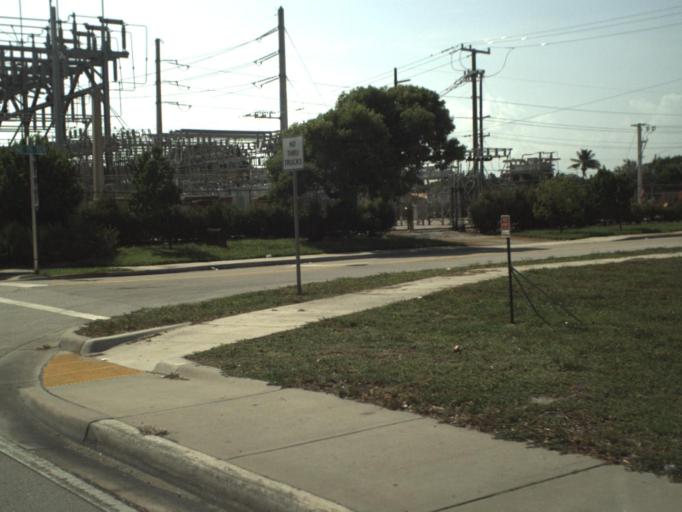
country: US
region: Florida
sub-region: Broward County
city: Pompano Beach Highlands
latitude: 26.2755
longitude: -80.1021
